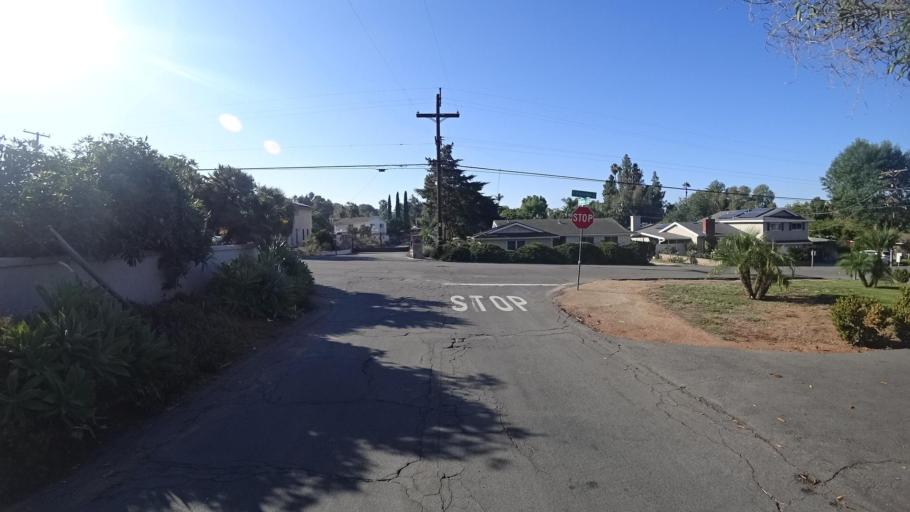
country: US
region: California
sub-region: San Diego County
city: Spring Valley
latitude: 32.7664
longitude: -116.9978
